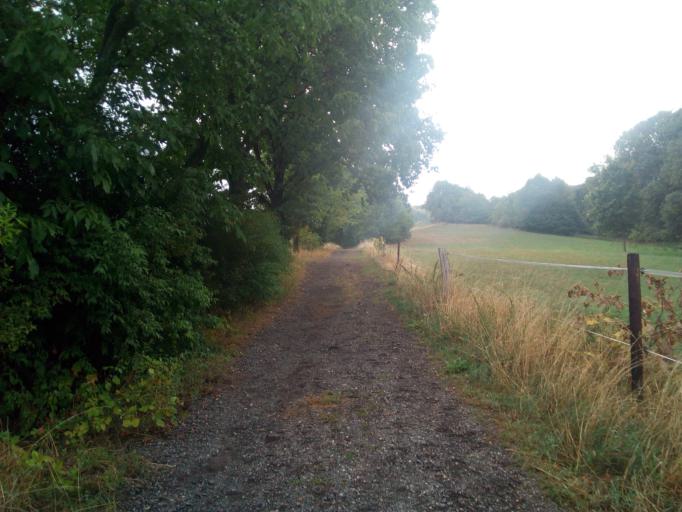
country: DE
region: Saxony
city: Kreischa
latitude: 50.9305
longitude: 13.7876
